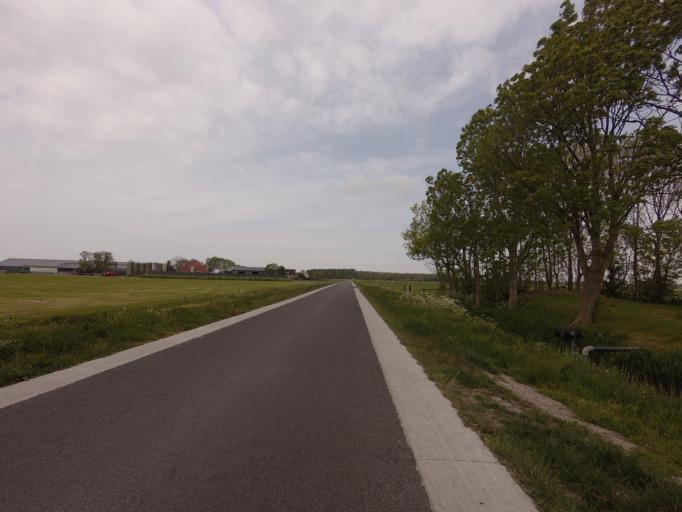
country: NL
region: Friesland
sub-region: Sudwest Fryslan
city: Bolsward
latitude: 53.0888
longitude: 5.4822
